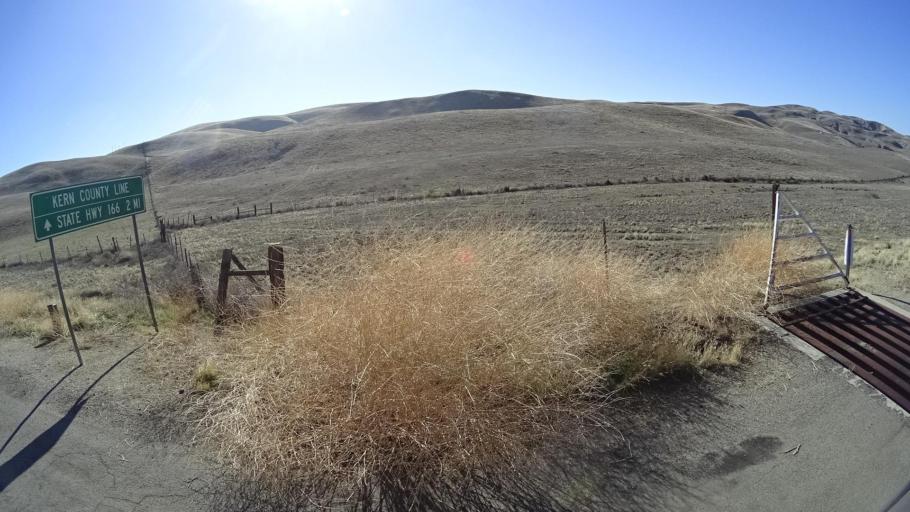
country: US
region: California
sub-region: Kern County
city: Maricopa
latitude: 34.9845
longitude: -119.4731
